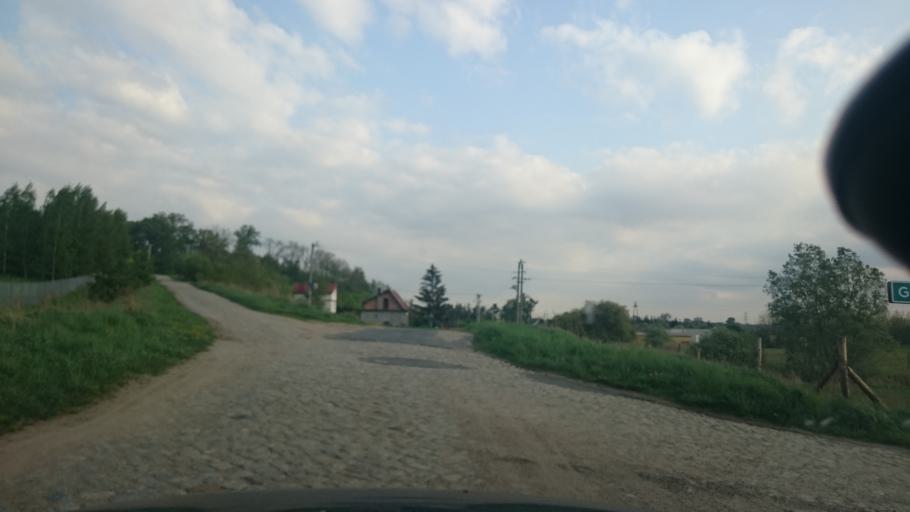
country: PL
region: Kujawsko-Pomorskie
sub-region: Grudziadz
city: Grudziadz
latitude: 53.4696
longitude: 18.8150
